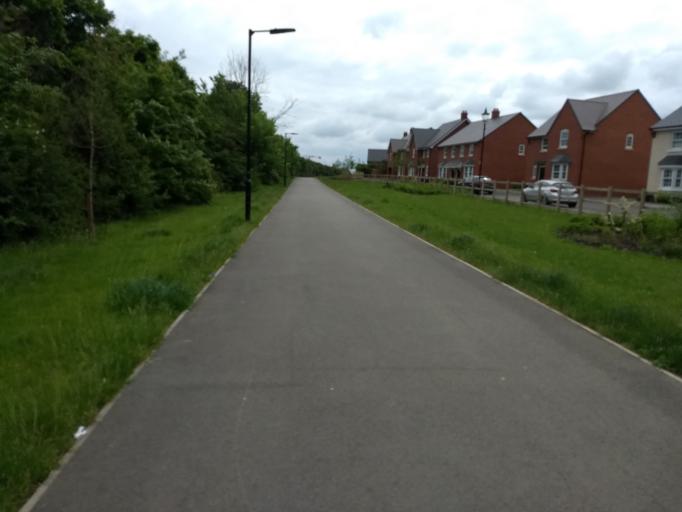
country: GB
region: England
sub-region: Bedford
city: Kempston
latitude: 52.1103
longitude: -0.5140
